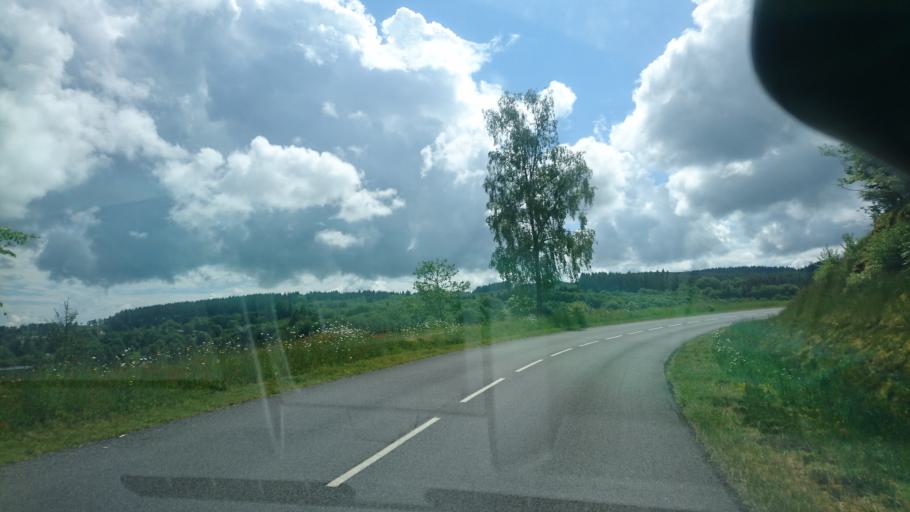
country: FR
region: Limousin
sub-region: Departement de la Haute-Vienne
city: Peyrat-le-Chateau
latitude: 45.7805
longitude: 1.8651
